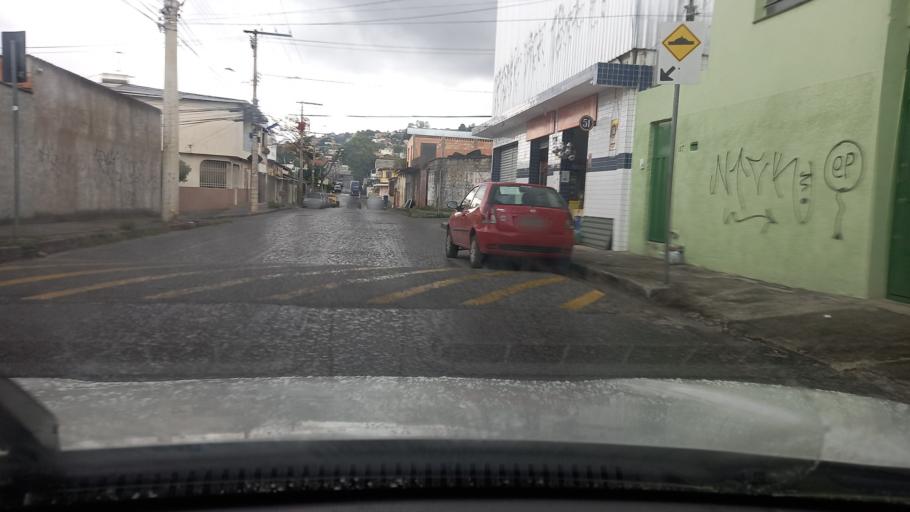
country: BR
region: Minas Gerais
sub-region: Contagem
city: Contagem
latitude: -19.8977
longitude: -44.0107
